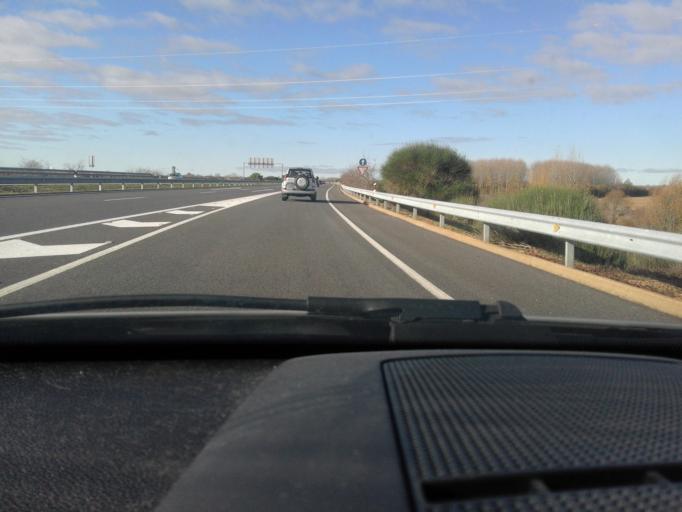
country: ES
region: Castille and Leon
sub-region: Provincia de Palencia
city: Carrion de los Condes
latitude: 42.3499
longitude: -4.6267
